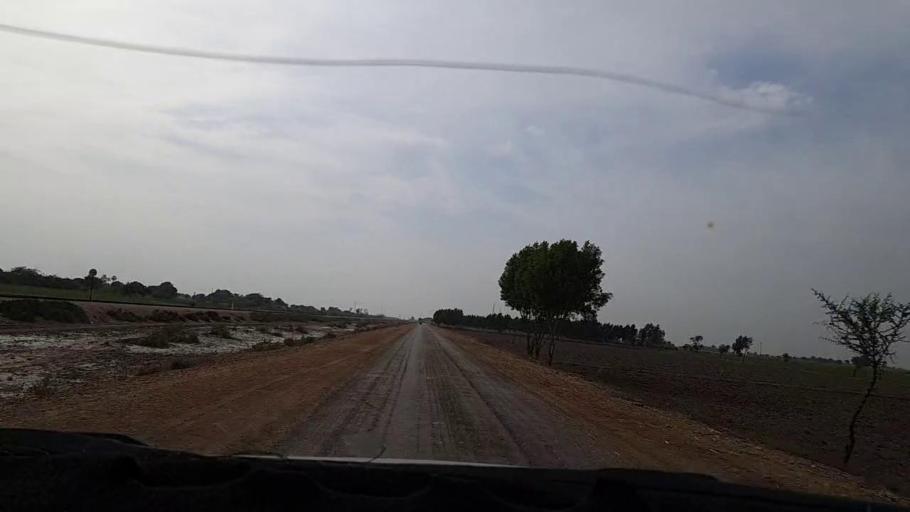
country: PK
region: Sindh
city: Pithoro
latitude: 25.5174
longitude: 69.2517
